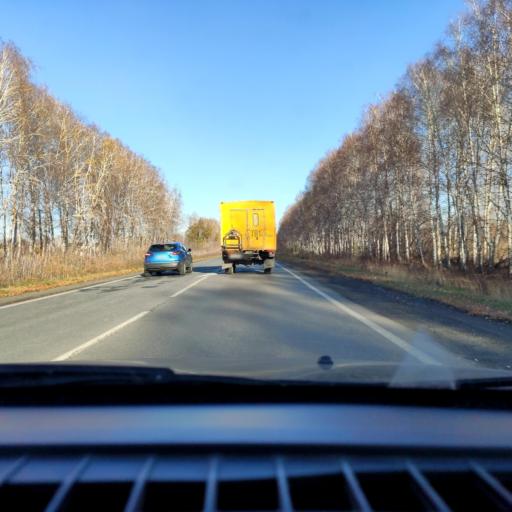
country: RU
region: Samara
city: Tol'yatti
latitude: 53.5939
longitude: 49.3271
